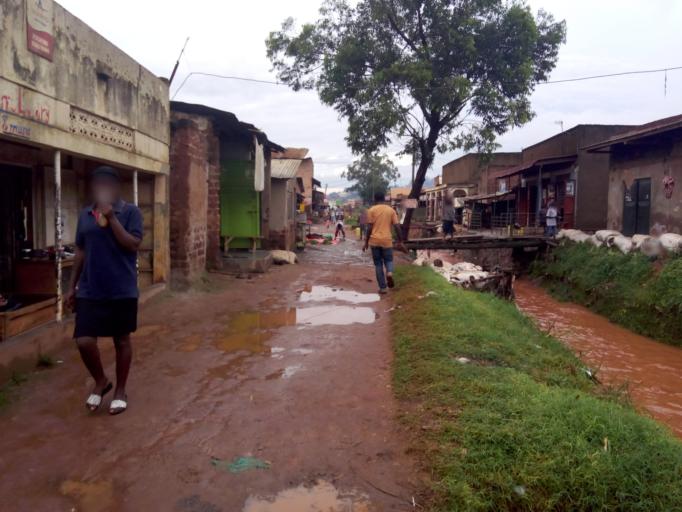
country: UG
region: Central Region
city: Kampala Central Division
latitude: 0.3356
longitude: 32.5593
